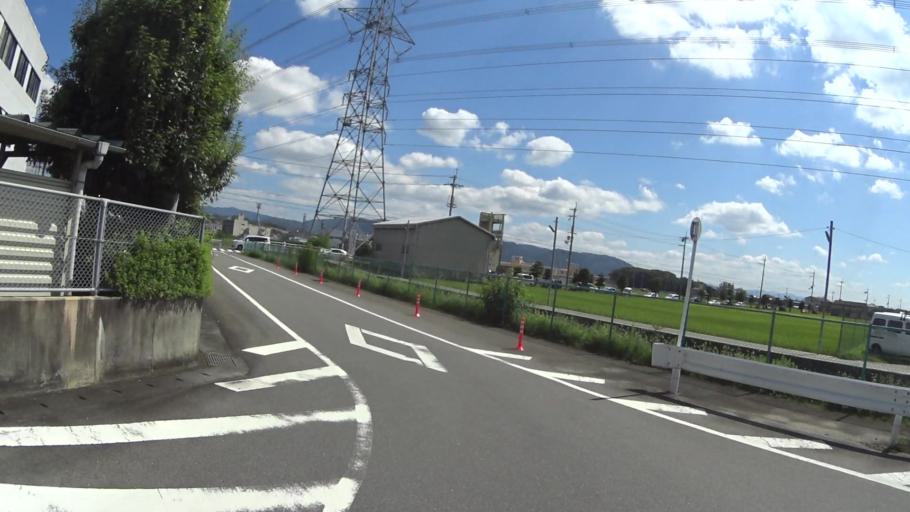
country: JP
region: Kyoto
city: Tanabe
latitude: 34.8462
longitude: 135.7795
